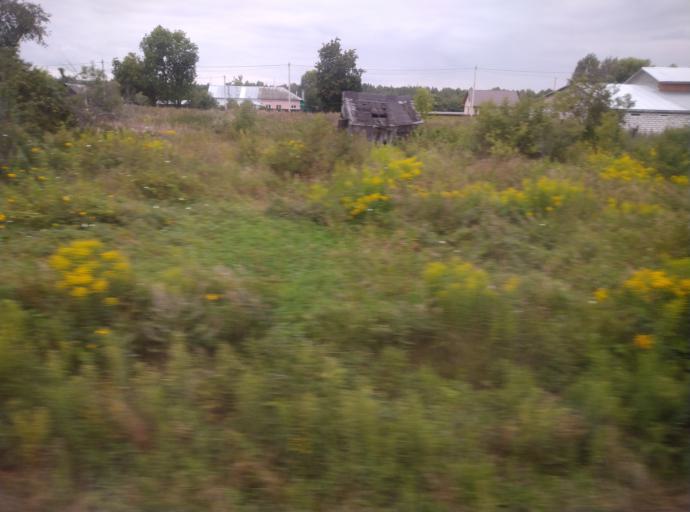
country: RU
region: Kostroma
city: Kosmynino
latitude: 57.5851
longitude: 40.7564
